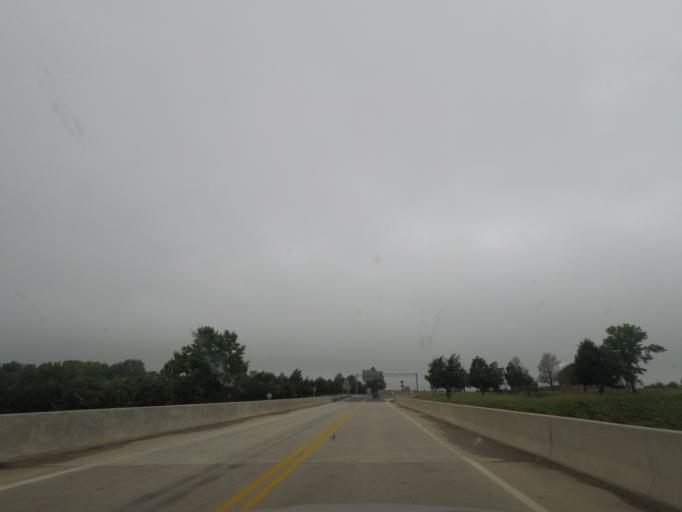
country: US
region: Virginia
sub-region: Charlotte County
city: Charlotte Court House
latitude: 37.0638
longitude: -78.4704
